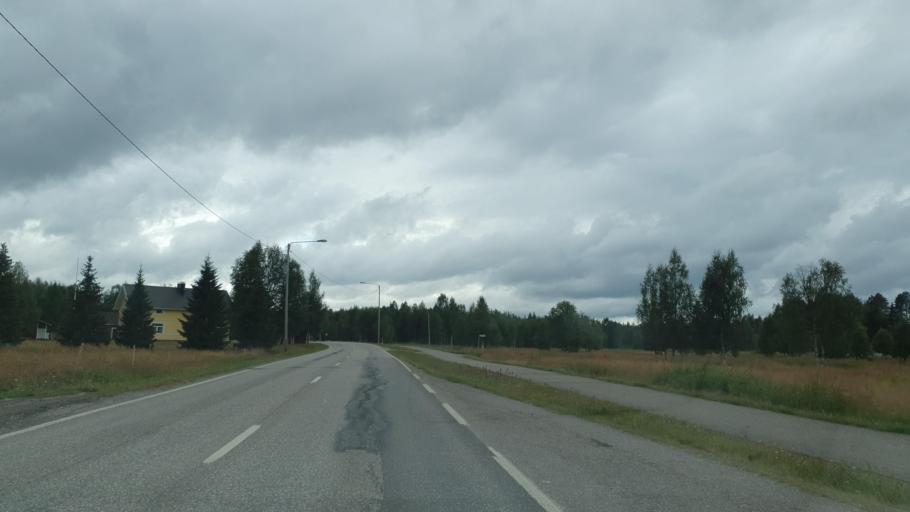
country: FI
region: Lapland
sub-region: Tunturi-Lappi
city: Kolari
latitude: 67.5228
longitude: 24.2957
